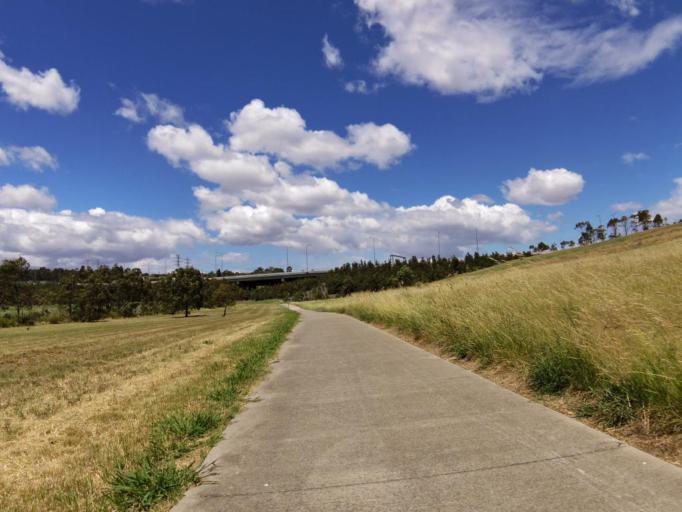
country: AU
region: Victoria
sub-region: Hume
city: Jacana
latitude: -37.6915
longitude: 144.9042
